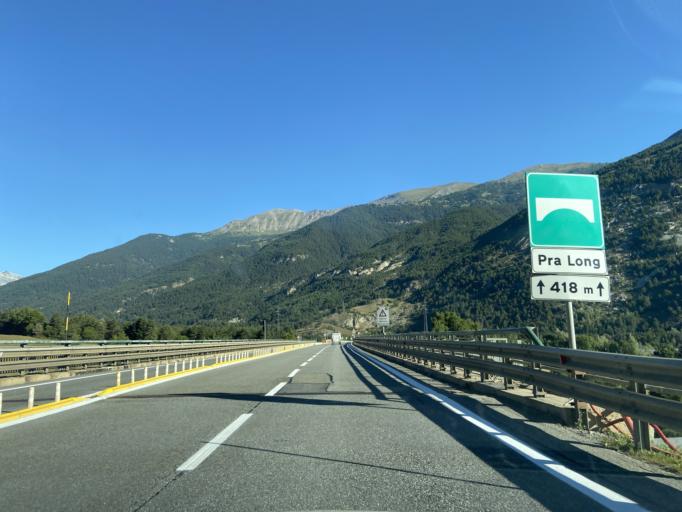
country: IT
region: Piedmont
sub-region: Provincia di Torino
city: Oulx
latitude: 45.0353
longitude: 6.8185
